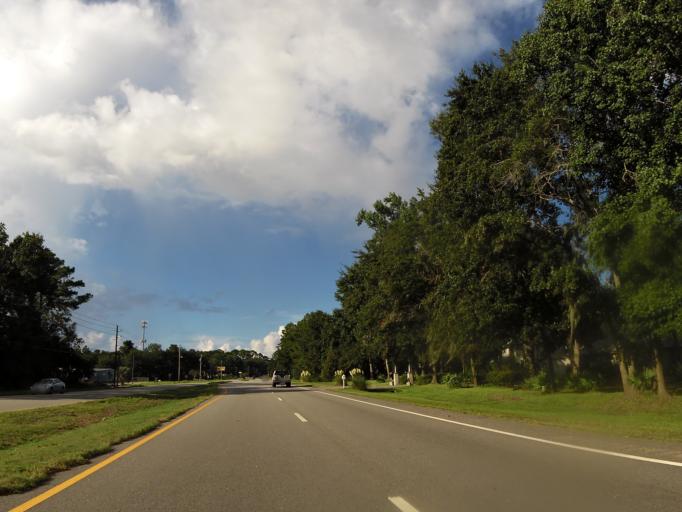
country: US
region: Georgia
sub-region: Glynn County
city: Country Club Estates
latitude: 31.2100
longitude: -81.4664
